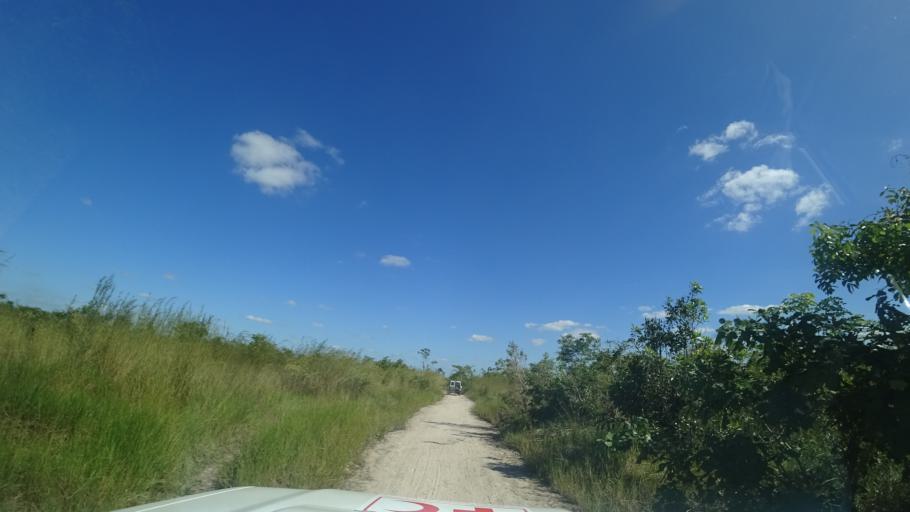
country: MZ
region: Sofala
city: Dondo
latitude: -19.4786
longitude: 34.6267
